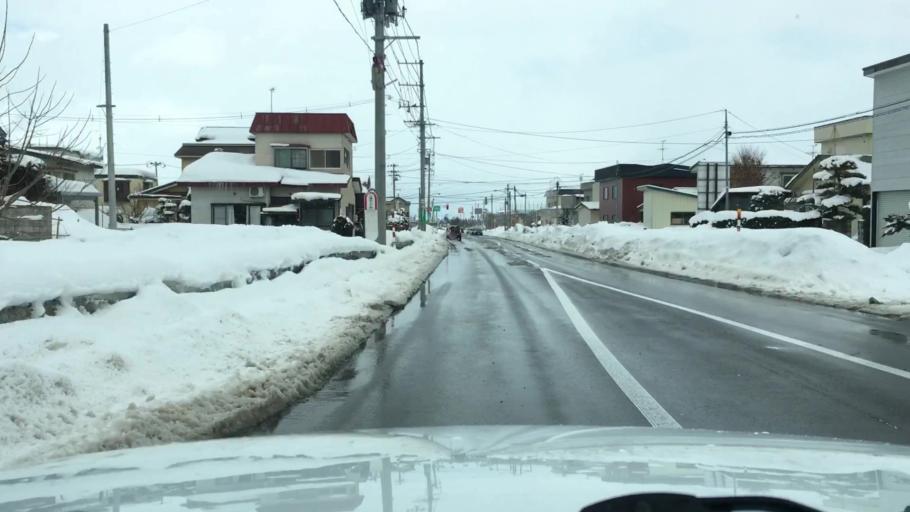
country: JP
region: Aomori
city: Hirosaki
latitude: 40.5809
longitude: 140.4961
